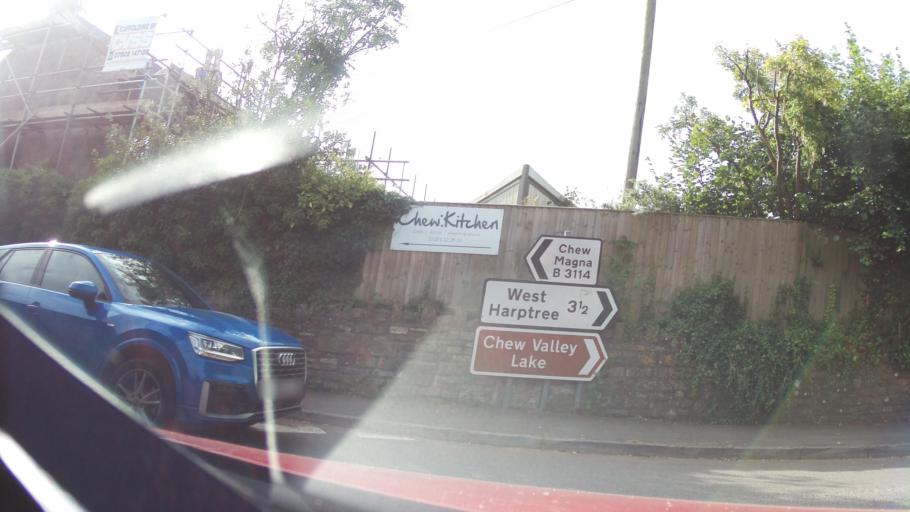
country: GB
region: England
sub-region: Bath and North East Somerset
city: Chew Magna
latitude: 51.3559
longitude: -2.6313
